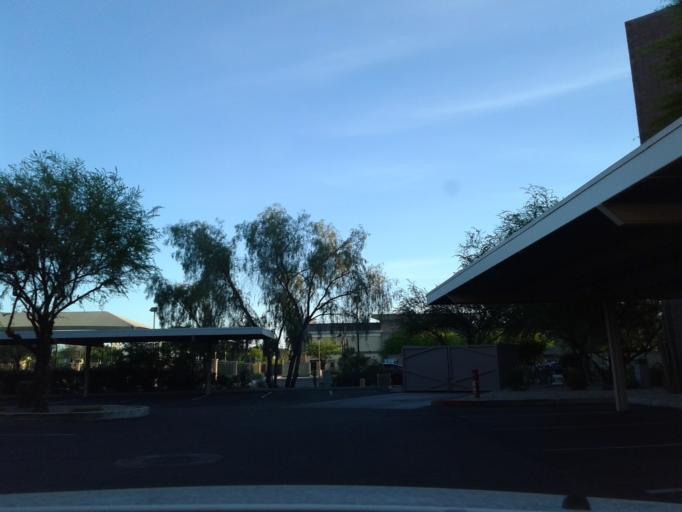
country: US
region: Arizona
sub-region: Maricopa County
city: Paradise Valley
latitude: 33.6211
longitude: -111.9245
